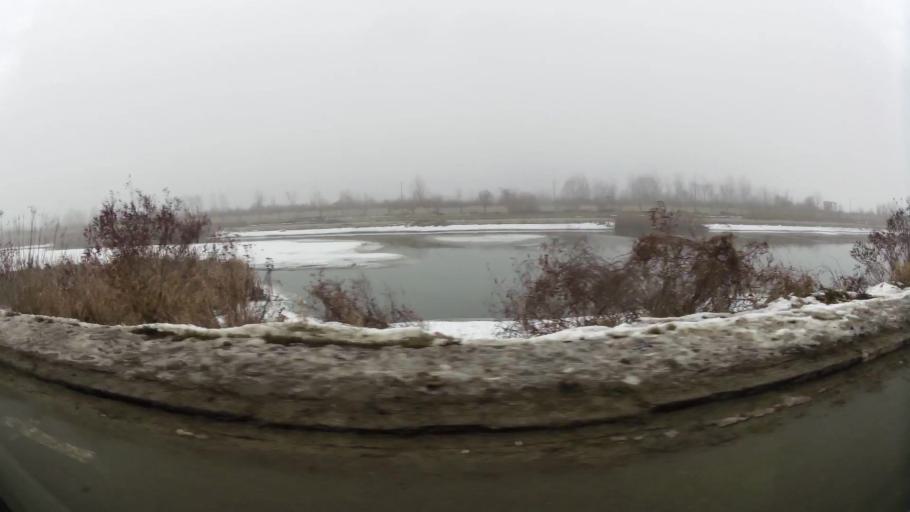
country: RO
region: Ilfov
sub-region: Comuna Chiajna
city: Chiajna
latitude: 44.4636
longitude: 25.9903
